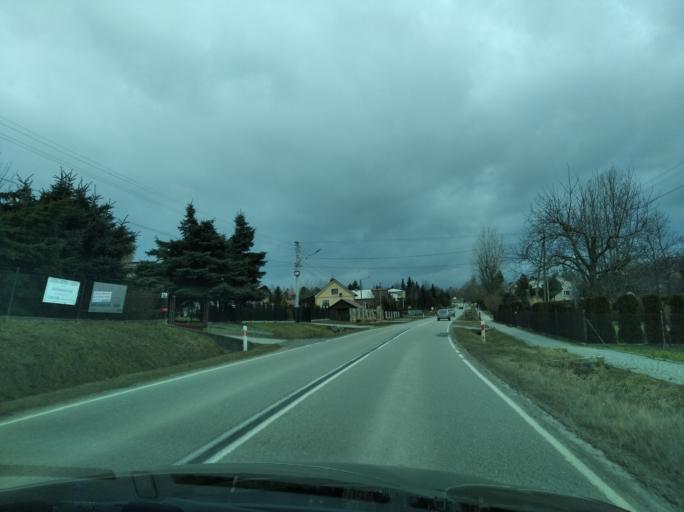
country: PL
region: Subcarpathian Voivodeship
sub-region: Powiat lancucki
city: Lancut
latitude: 50.0454
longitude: 22.2270
